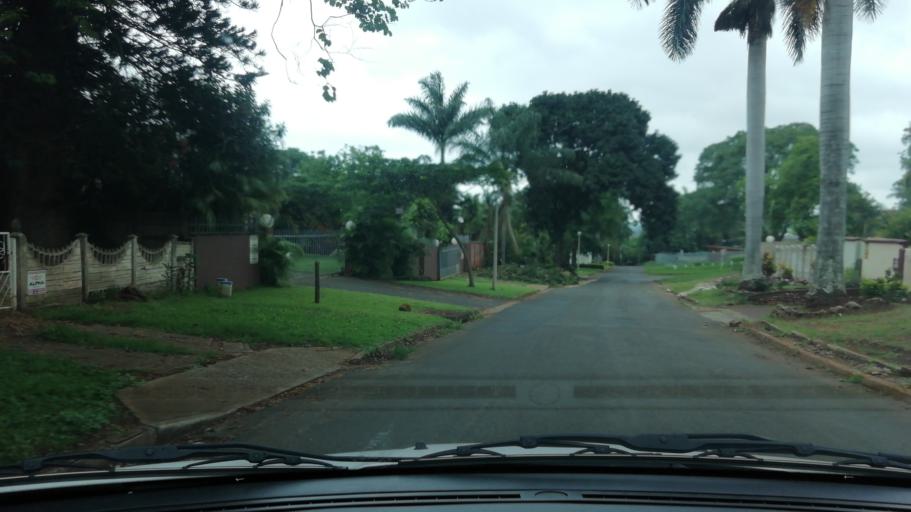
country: ZA
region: KwaZulu-Natal
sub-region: uThungulu District Municipality
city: Empangeni
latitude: -28.7648
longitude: 31.8947
